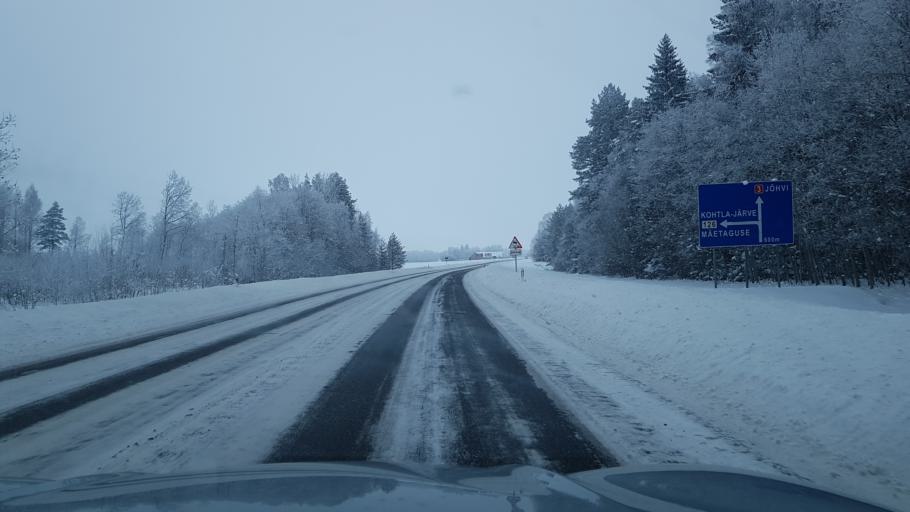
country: EE
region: Ida-Virumaa
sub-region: Johvi vald
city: Johvi
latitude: 59.2214
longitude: 27.3374
